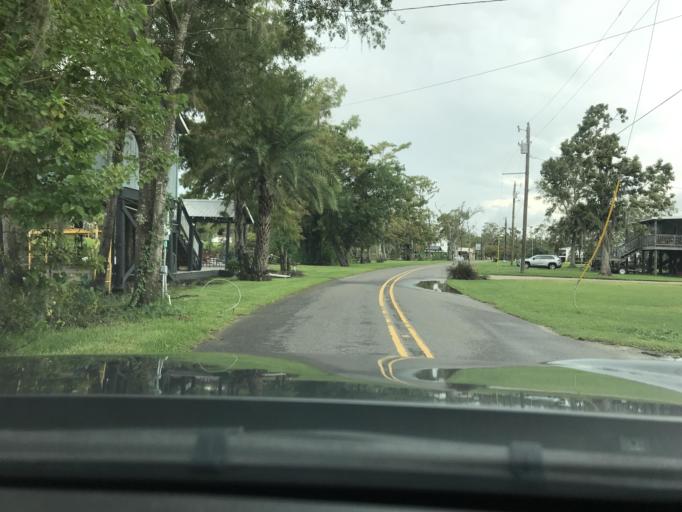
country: US
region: Louisiana
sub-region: Calcasieu Parish
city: Westlake
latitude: 30.2750
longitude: -93.2266
